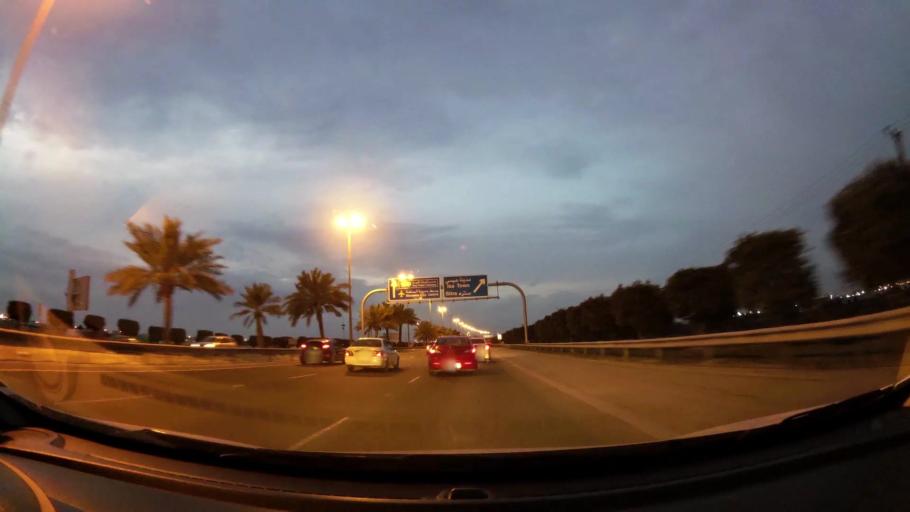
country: BH
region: Northern
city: Madinat `Isa
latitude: 26.1704
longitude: 50.5028
